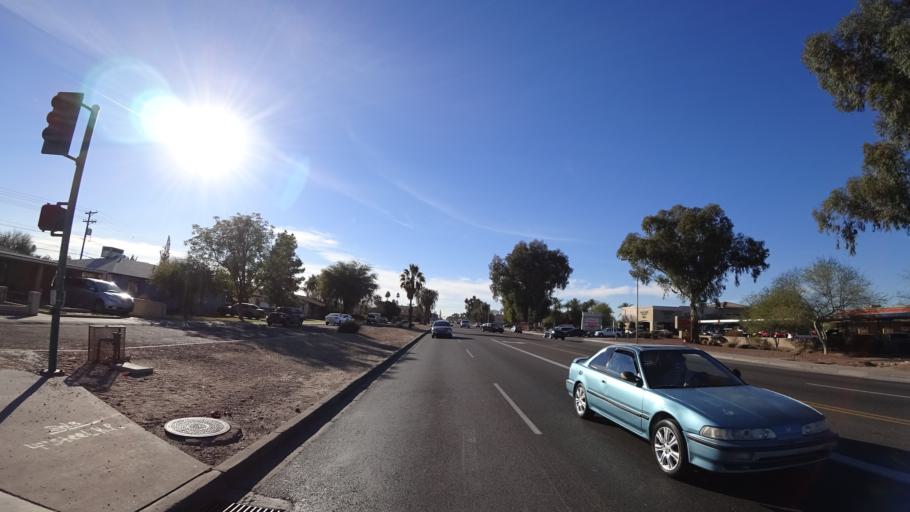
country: US
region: Arizona
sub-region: Maricopa County
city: Glendale
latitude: 33.5239
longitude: -112.1302
